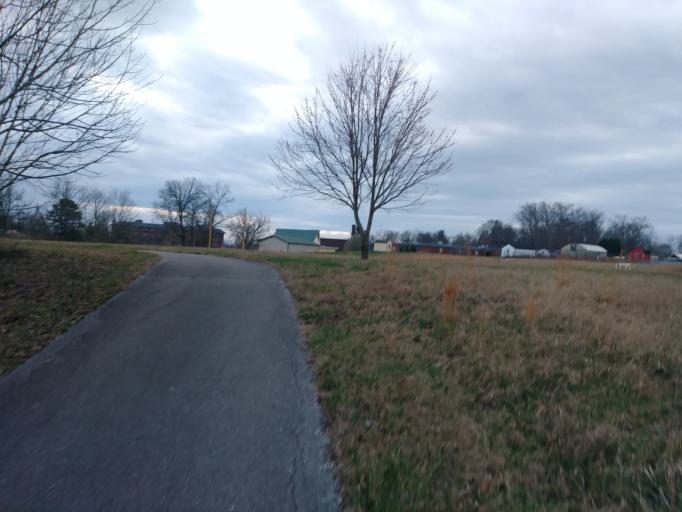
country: US
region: Tennessee
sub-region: Greene County
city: Tusculum
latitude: 36.1787
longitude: -82.7555
